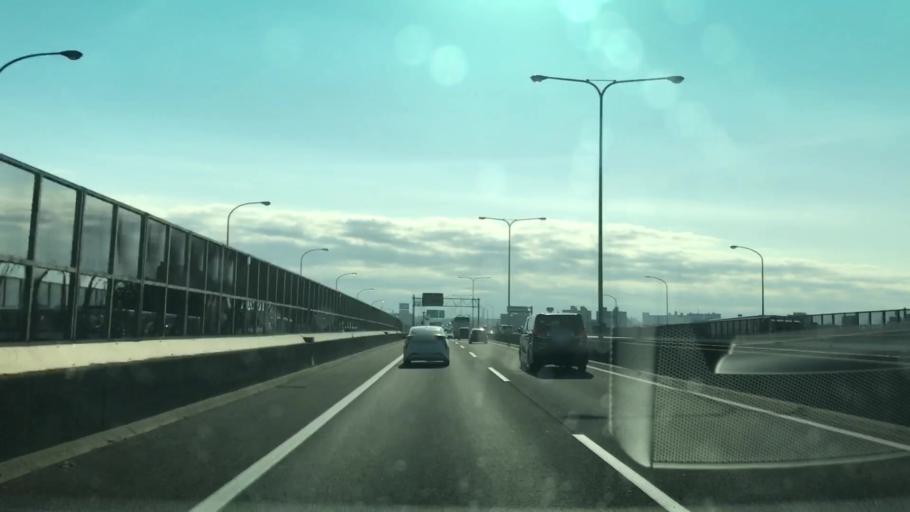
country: JP
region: Hokkaido
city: Sapporo
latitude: 43.0463
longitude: 141.4346
